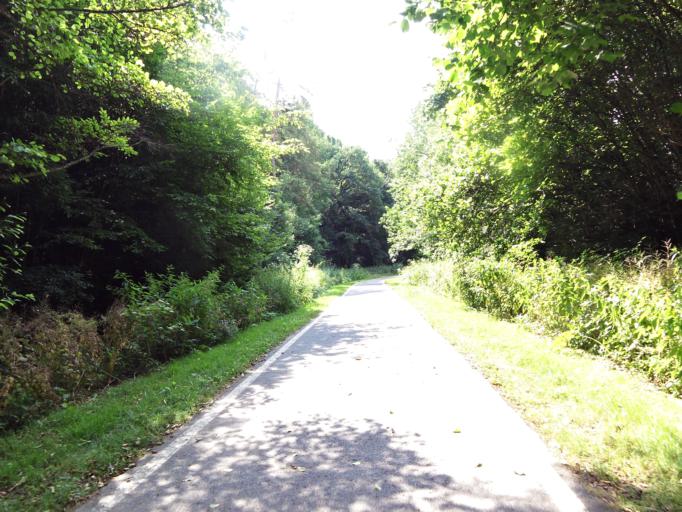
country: DE
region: Bavaria
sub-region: Regierungsbezirk Unterfranken
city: Reichenberg
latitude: 49.7424
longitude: 9.9484
